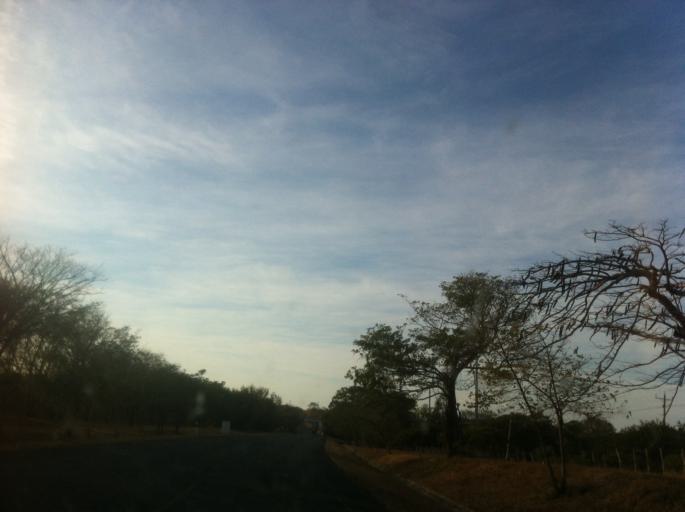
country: NI
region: Rivas
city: Rivas
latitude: 11.3735
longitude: -85.7583
